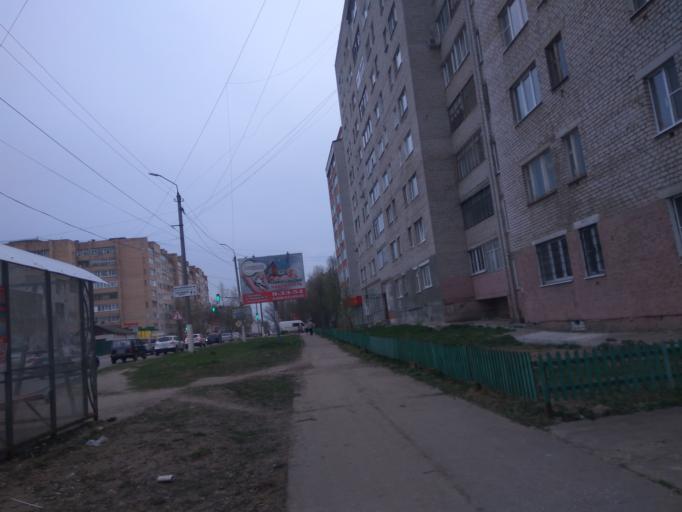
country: RU
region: Vladimir
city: Aleksandrov
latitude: 56.4012
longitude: 38.7131
